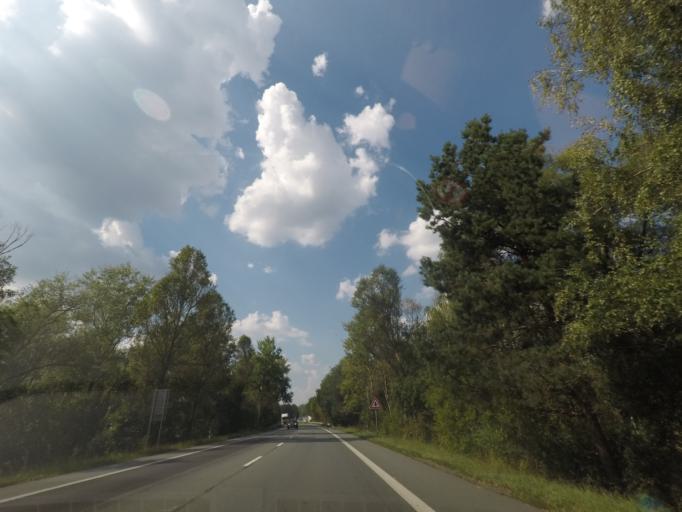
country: CZ
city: Tyniste nad Orlici
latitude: 50.1536
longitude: 16.0676
